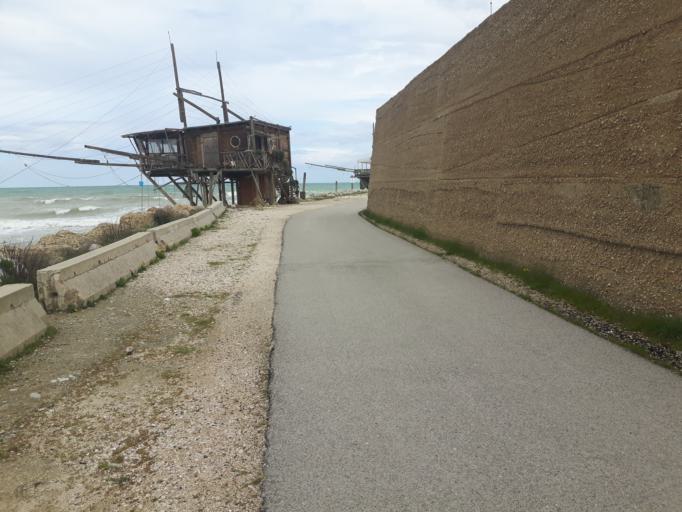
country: IT
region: Abruzzo
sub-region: Provincia di Chieti
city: Vasto
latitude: 42.1748
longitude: 14.7083
